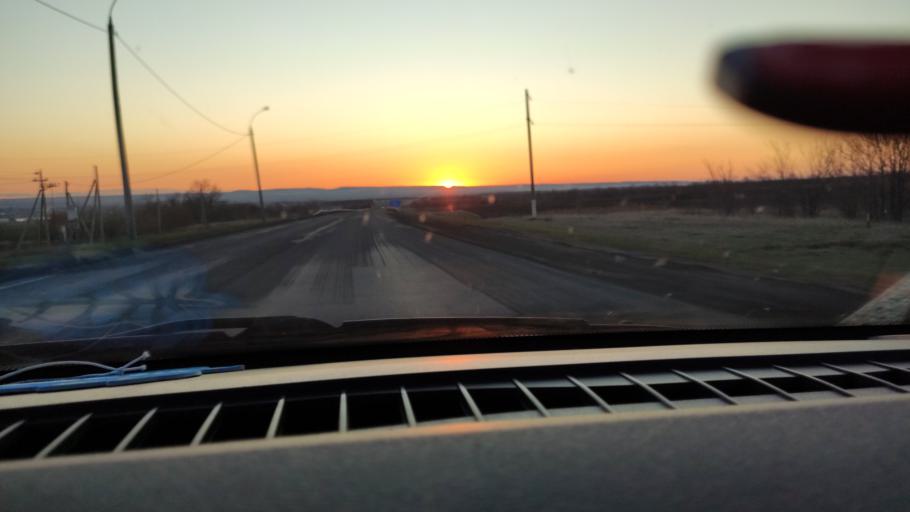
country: RU
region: Saratov
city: Yelshanka
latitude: 51.7923
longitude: 46.1574
